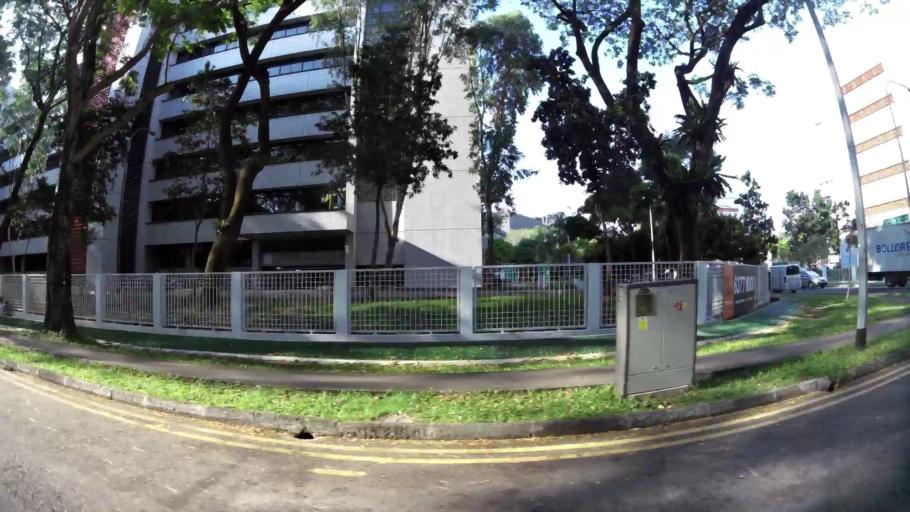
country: SG
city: Singapore
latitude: 1.3272
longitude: 103.8731
